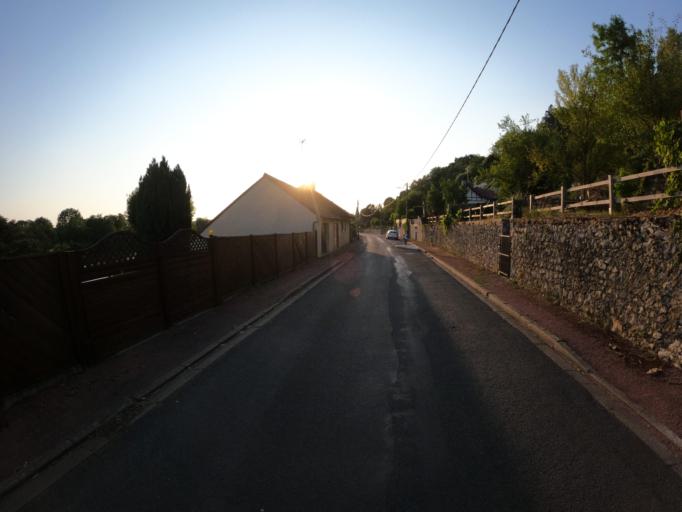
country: FR
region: Pays de la Loire
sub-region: Departement de la Sarthe
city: Parce-sur-Sarthe
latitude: 47.8645
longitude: -0.2029
